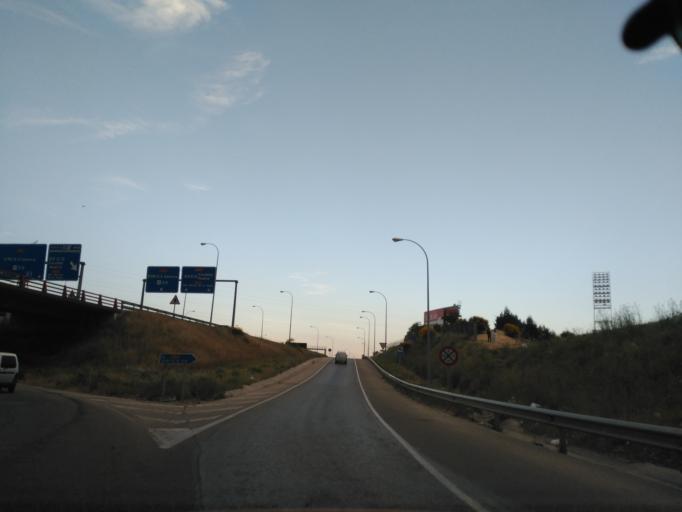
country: ES
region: Madrid
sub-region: Provincia de Madrid
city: Getafe
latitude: 40.3273
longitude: -3.7176
